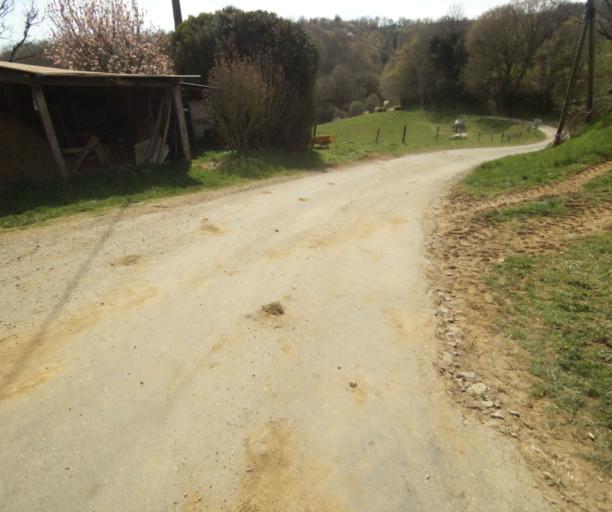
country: FR
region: Limousin
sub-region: Departement de la Correze
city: Naves
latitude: 45.3744
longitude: 1.7834
